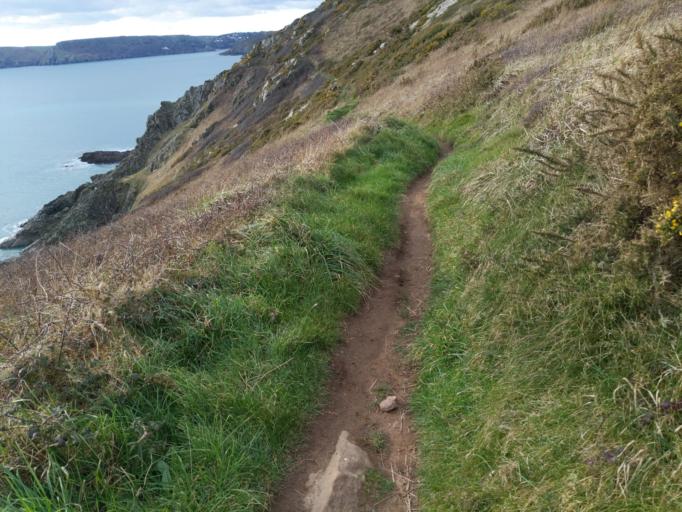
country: GB
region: England
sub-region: Devon
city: Salcombe
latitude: 50.2101
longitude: -3.7310
